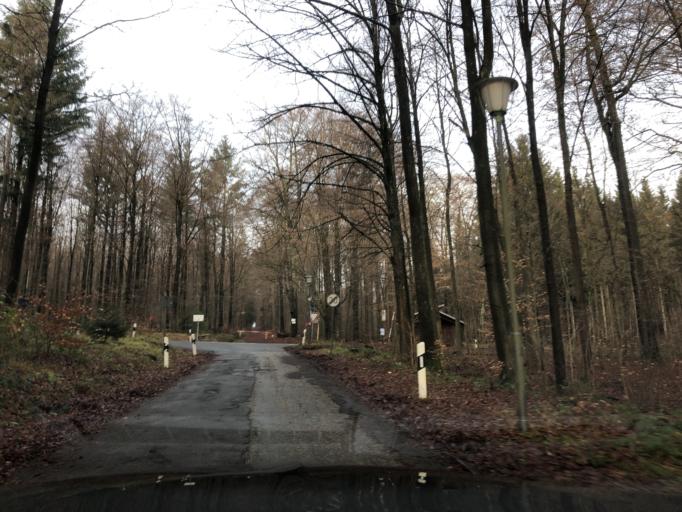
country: DE
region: Baden-Wuerttemberg
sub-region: Karlsruhe Region
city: Gaiberg
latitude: 49.3879
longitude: 8.7320
